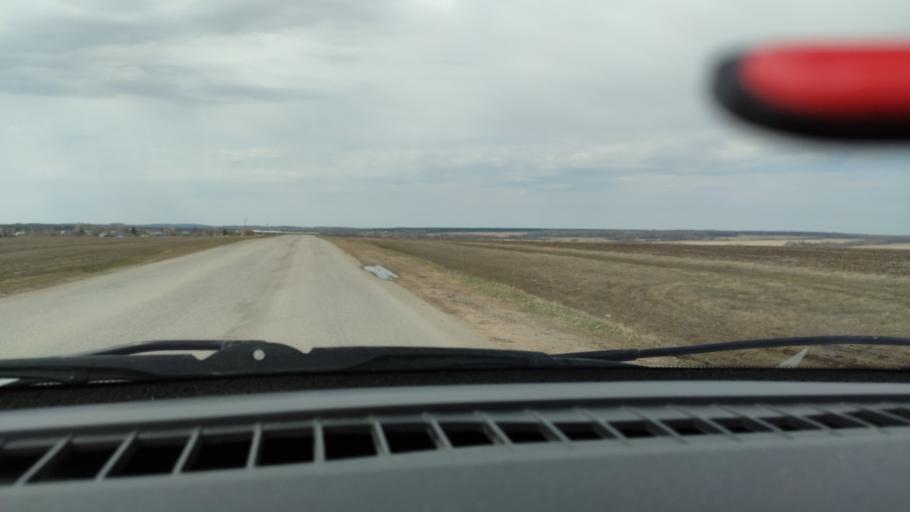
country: RU
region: Bashkortostan
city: Dyurtyuli
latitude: 55.6569
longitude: 55.0375
